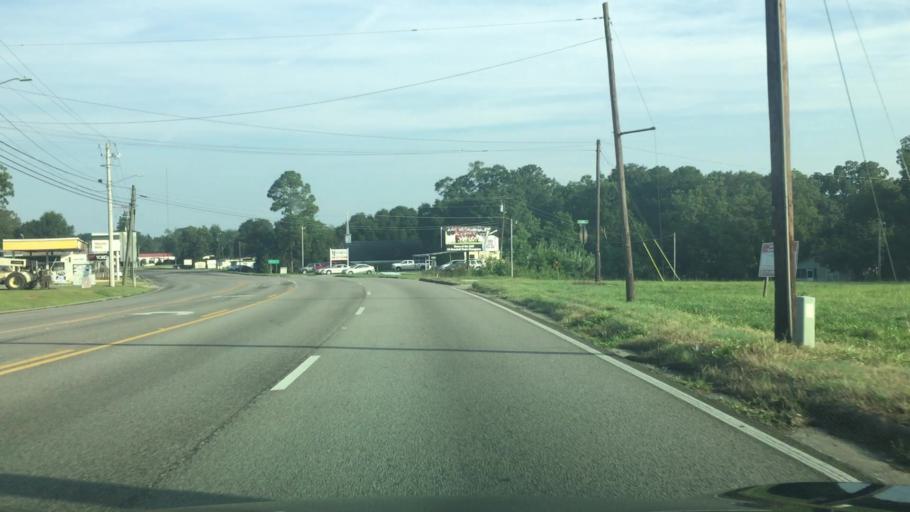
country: US
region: Alabama
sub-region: Covington County
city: Andalusia
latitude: 31.3184
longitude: -86.4983
